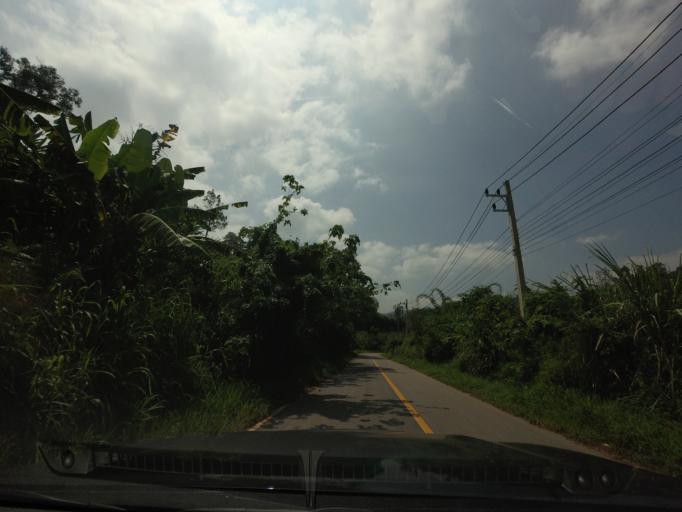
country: TH
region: Loei
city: Na Haeo
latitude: 17.4747
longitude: 100.9399
